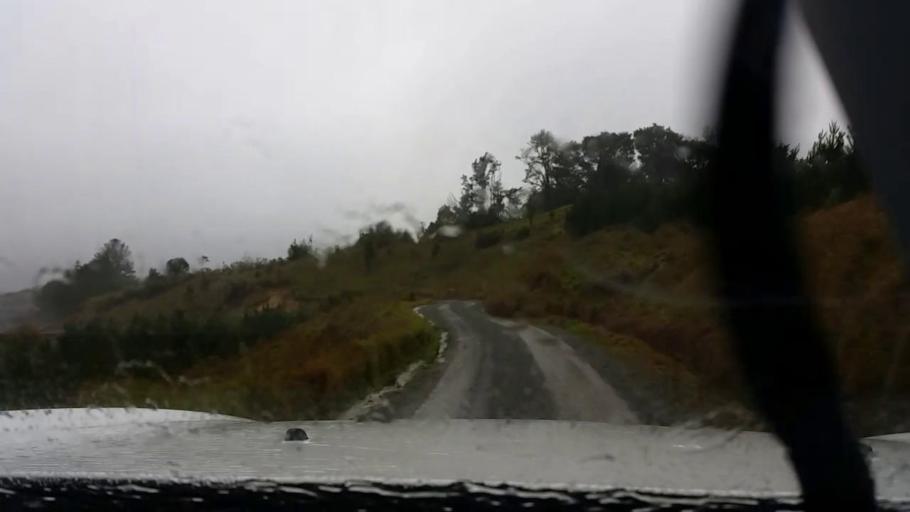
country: NZ
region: Wellington
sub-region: Masterton District
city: Masterton
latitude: -41.2006
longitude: 175.8105
